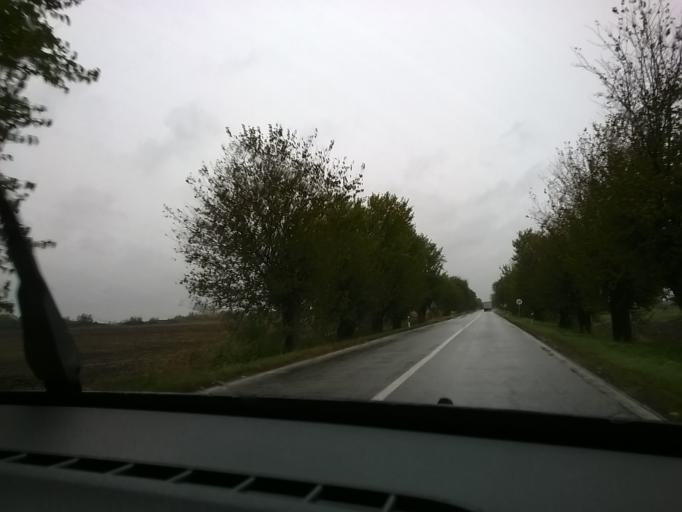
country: RS
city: Pavlis
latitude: 45.0212
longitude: 21.2784
